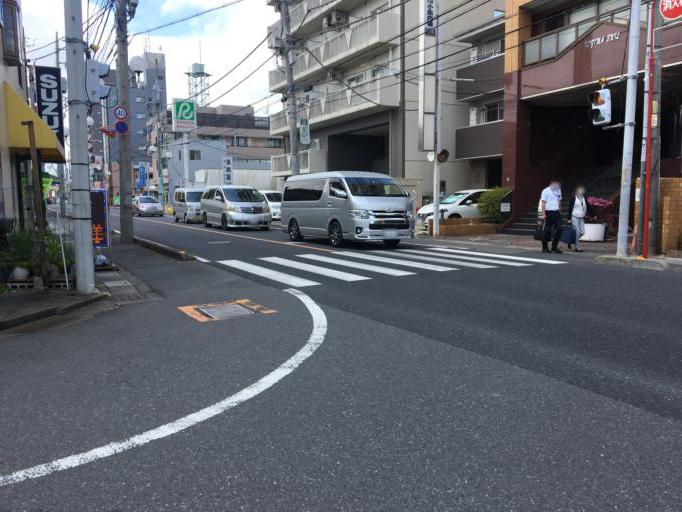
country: JP
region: Saitama
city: Okegawa
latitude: 35.9982
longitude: 139.5679
